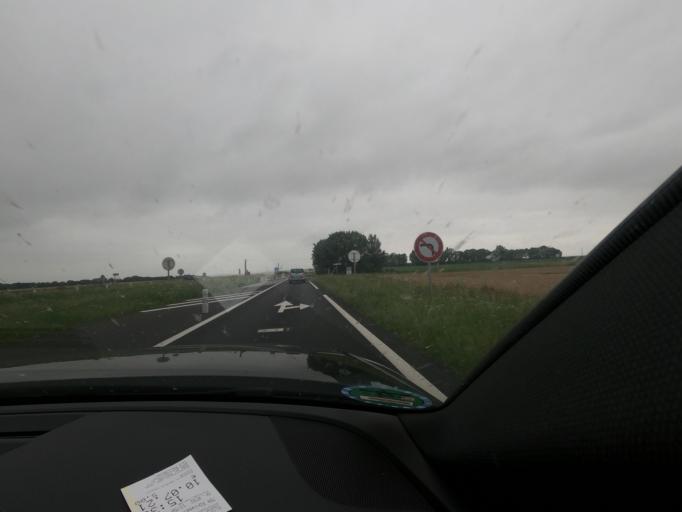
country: FR
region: Picardie
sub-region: Departement de la Somme
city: Boves
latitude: 49.8317
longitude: 2.4550
